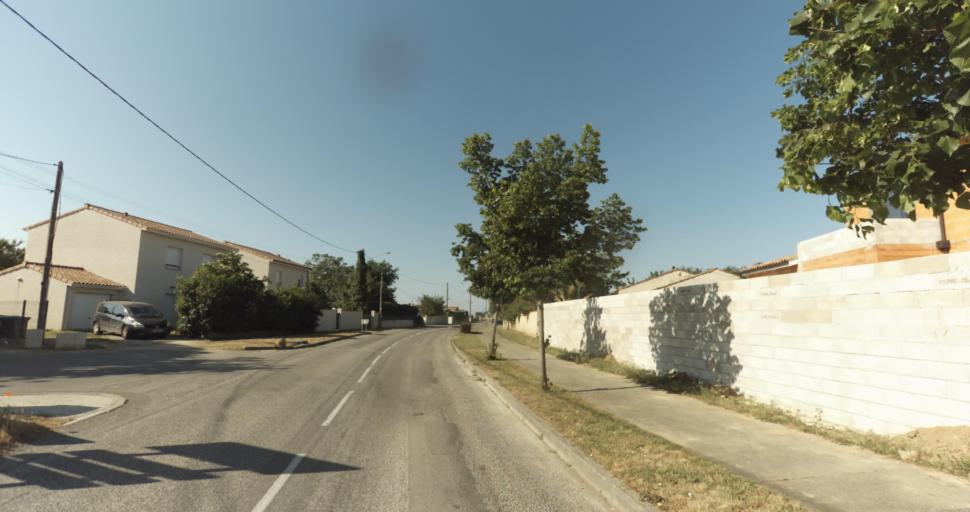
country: FR
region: Midi-Pyrenees
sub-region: Departement de la Haute-Garonne
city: Plaisance-du-Touch
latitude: 43.5544
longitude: 1.2957
